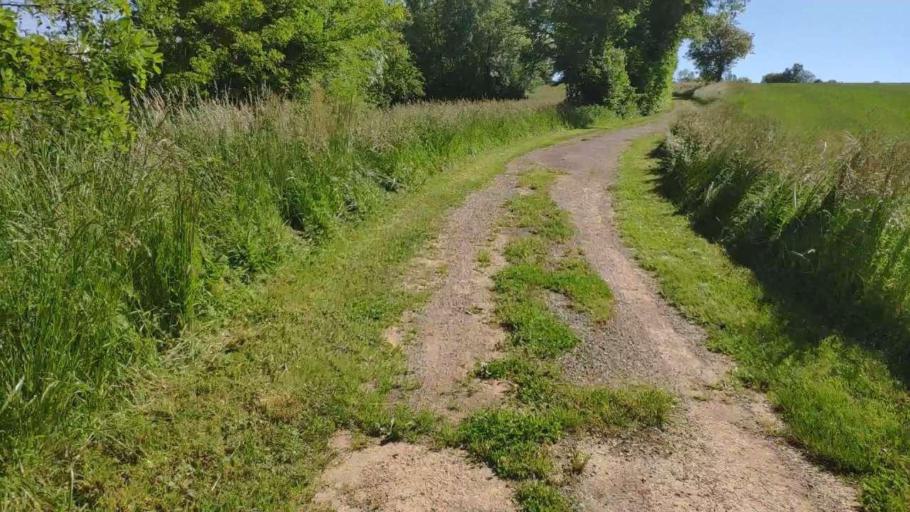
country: FR
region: Franche-Comte
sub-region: Departement du Jura
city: Perrigny
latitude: 46.7216
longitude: 5.5875
